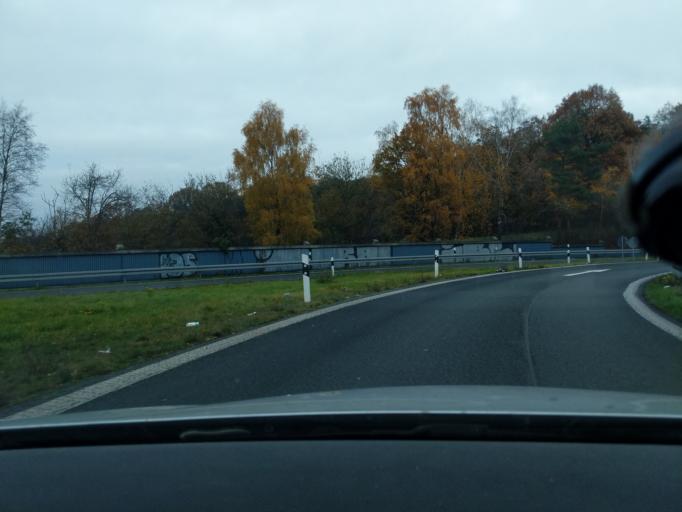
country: DE
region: North Rhine-Westphalia
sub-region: Regierungsbezirk Munster
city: Horstel
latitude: 52.2882
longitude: 7.5987
